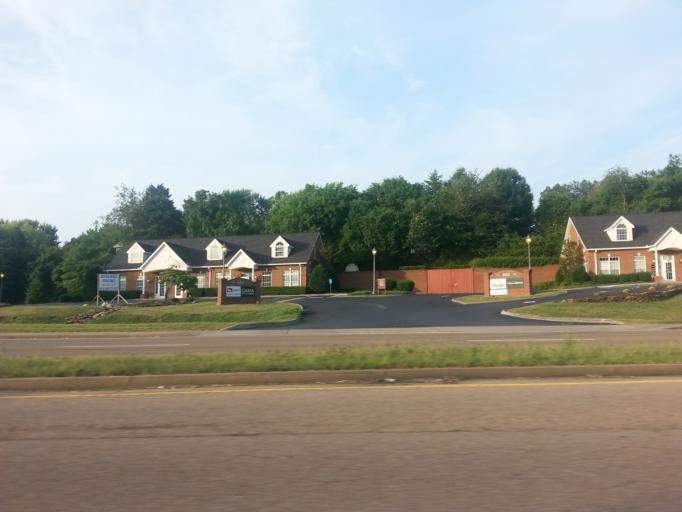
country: US
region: Tennessee
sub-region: Knox County
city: Farragut
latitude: 35.9434
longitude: -84.0959
